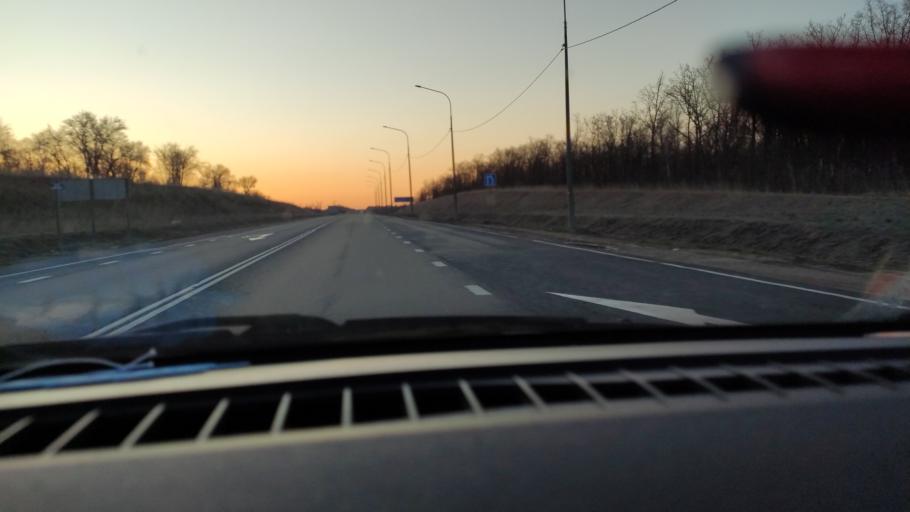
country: RU
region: Saratov
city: Yelshanka
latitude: 51.8245
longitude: 46.3027
